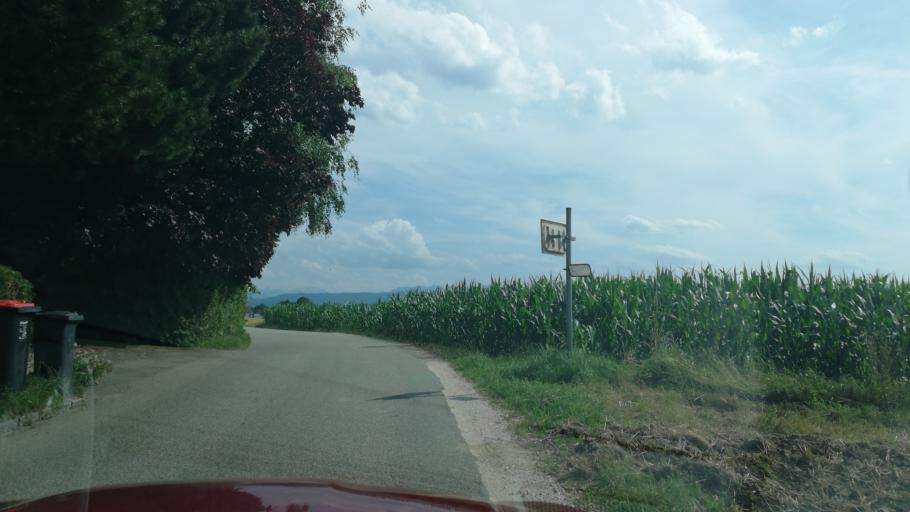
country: AT
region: Upper Austria
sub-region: Politischer Bezirk Vocklabruck
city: Puhret
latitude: 48.0357
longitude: 13.7031
